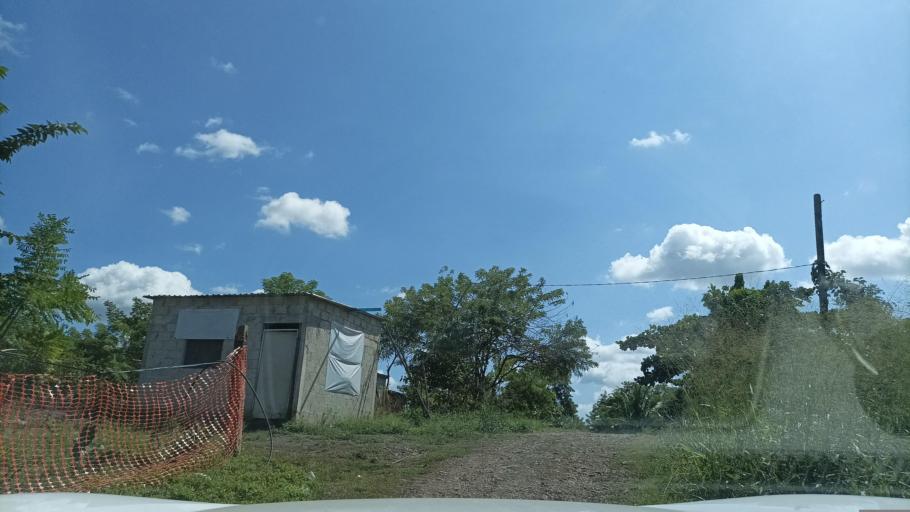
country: MX
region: Veracruz
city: Manlio Fabio Altamirano
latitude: 19.0882
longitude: -96.3422
